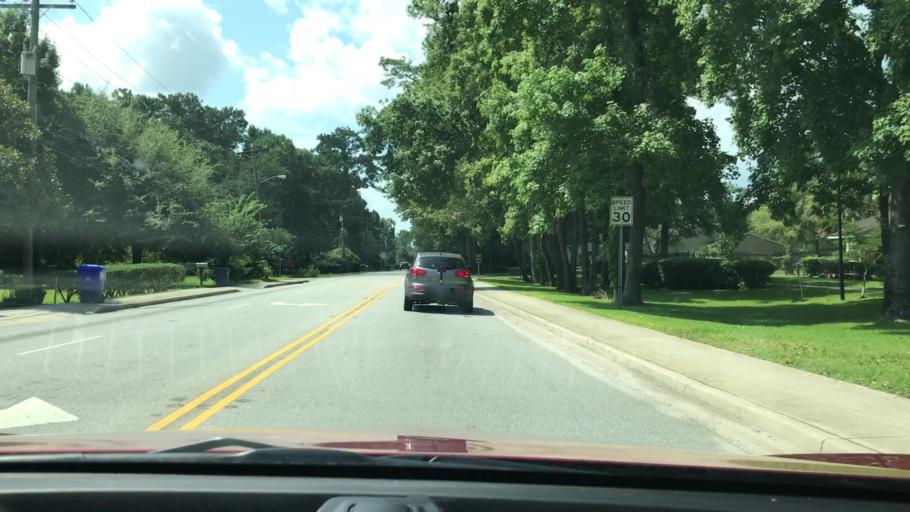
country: US
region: South Carolina
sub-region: Charleston County
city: North Charleston
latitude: 32.8059
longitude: -80.0298
